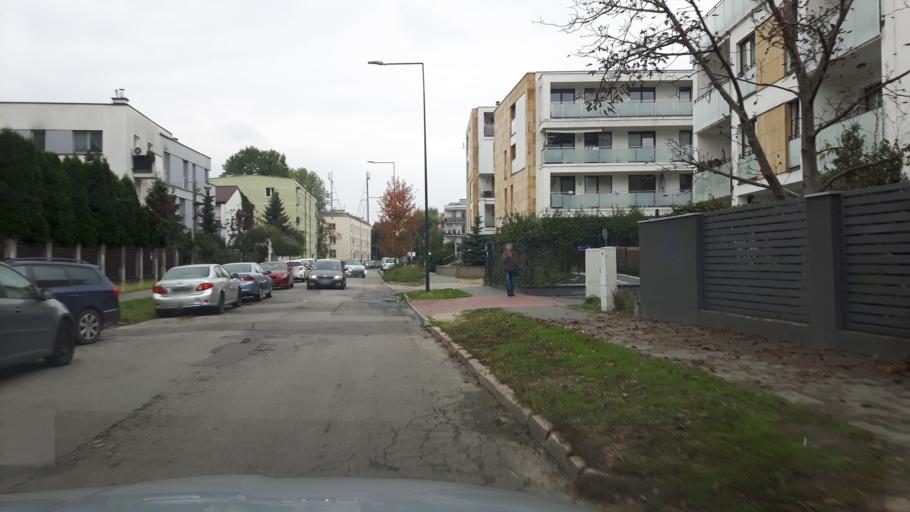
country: PL
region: Masovian Voivodeship
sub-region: Warszawa
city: Praga Poludnie
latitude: 52.2487
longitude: 21.1019
